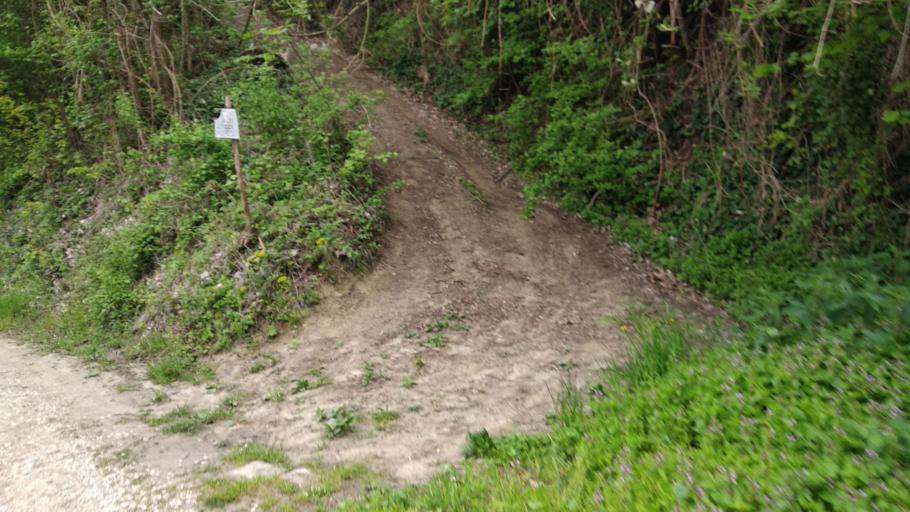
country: IT
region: Emilia-Romagna
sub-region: Forli-Cesena
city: Modigliana
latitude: 44.1492
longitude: 11.7971
